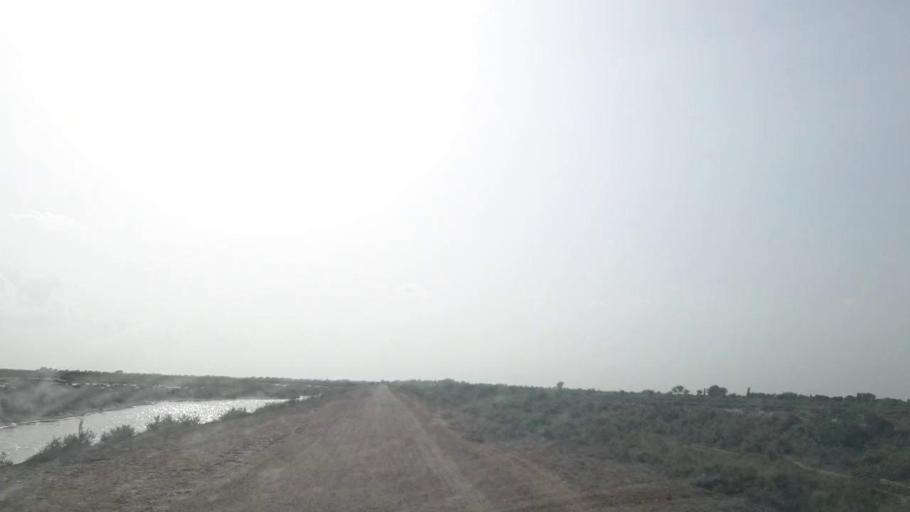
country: PK
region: Sindh
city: Tando Bago
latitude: 24.8153
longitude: 69.1482
